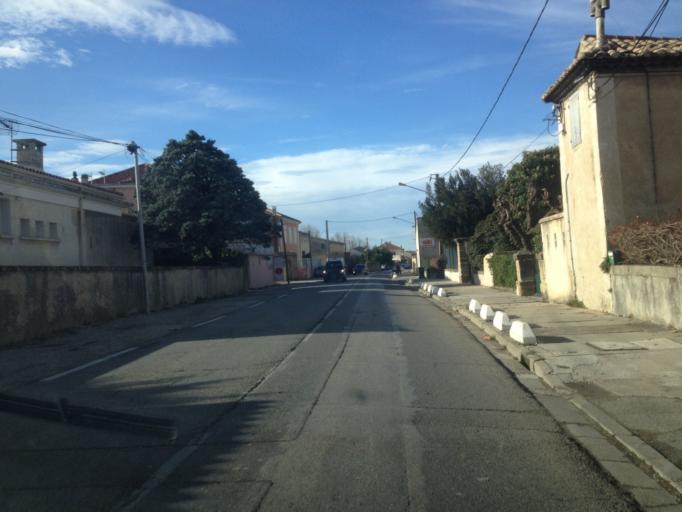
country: FR
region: Provence-Alpes-Cote d'Azur
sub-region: Departement du Vaucluse
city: Jonquieres
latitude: 44.1157
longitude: 4.8953
